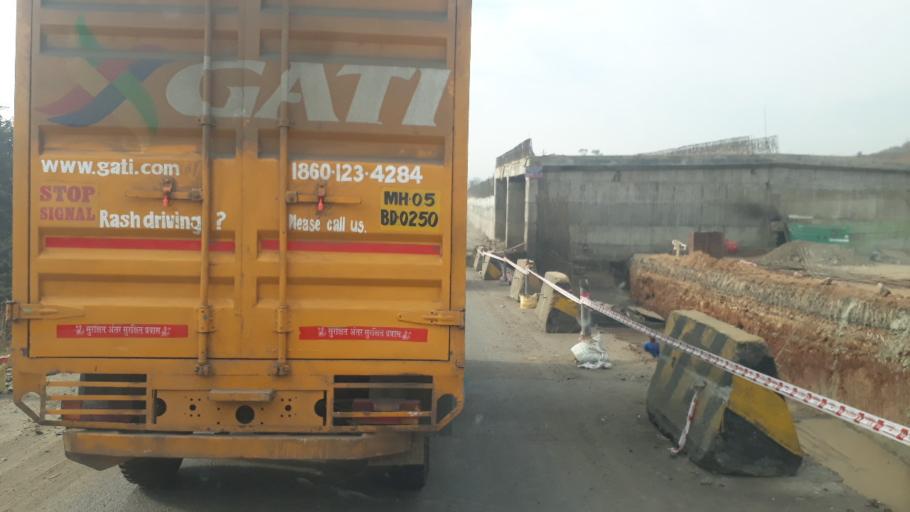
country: IN
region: Maharashtra
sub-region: Raigarh
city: Pen
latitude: 18.7726
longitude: 73.0930
